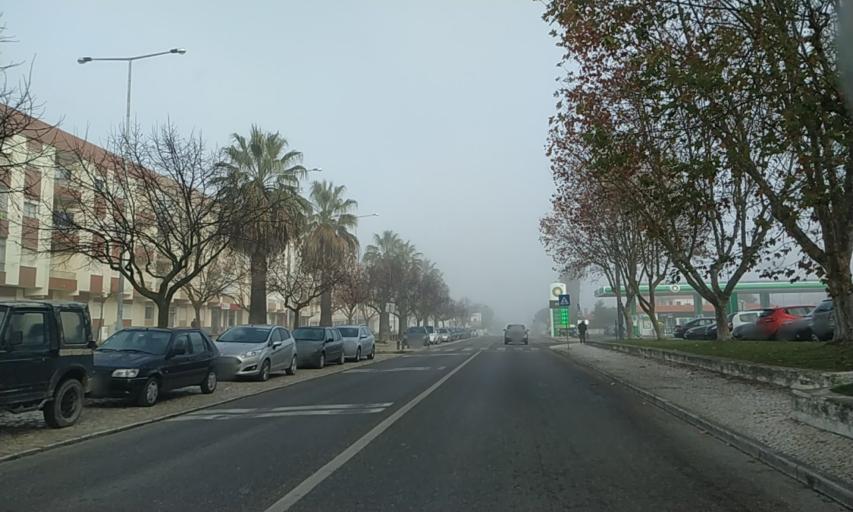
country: PT
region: Setubal
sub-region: Palmela
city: Pinhal Novo
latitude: 38.6357
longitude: -8.9146
